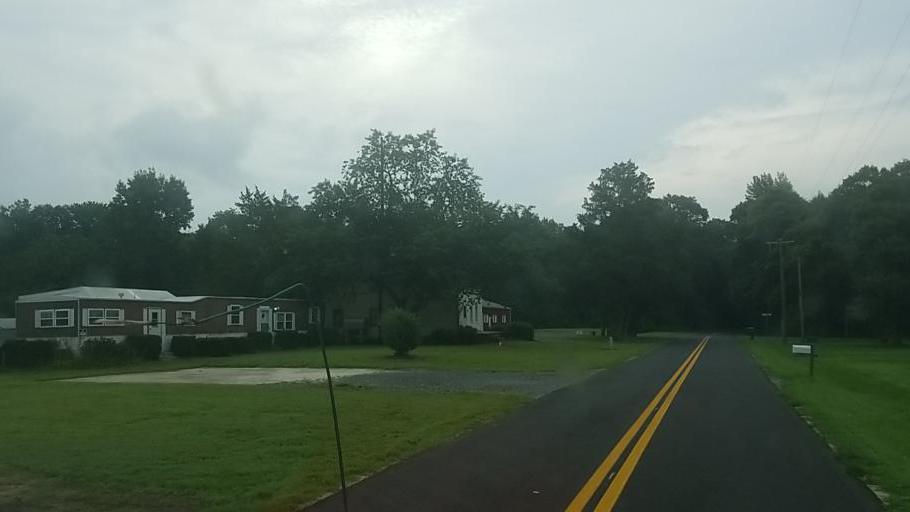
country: US
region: Delaware
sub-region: Sussex County
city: Selbyville
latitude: 38.4365
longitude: -75.2508
